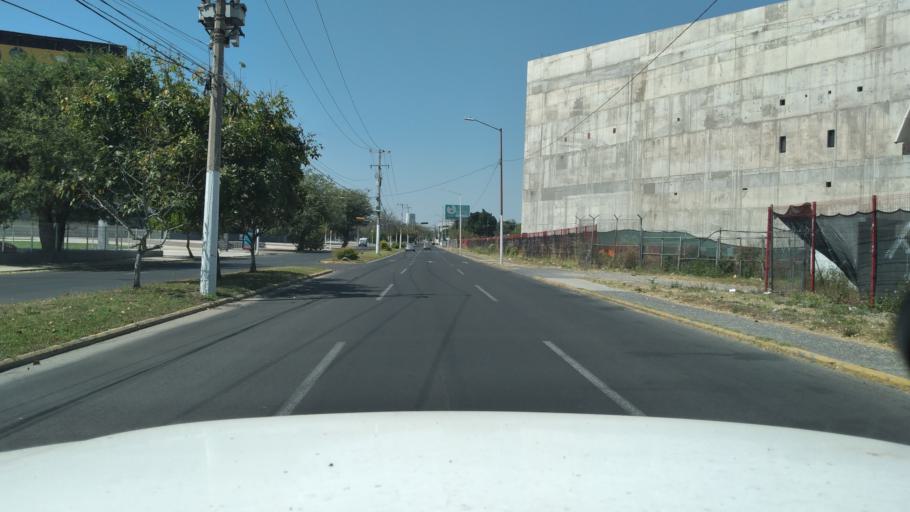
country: MX
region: Jalisco
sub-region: Zapopan
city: Zapopan
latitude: 20.7351
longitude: -103.3801
